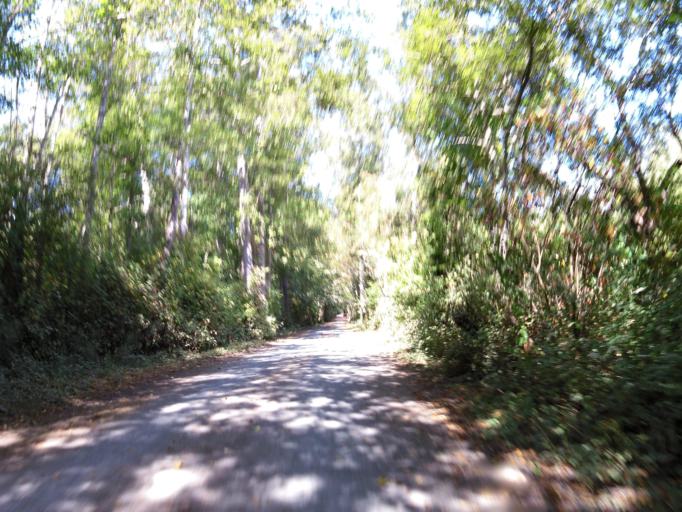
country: CA
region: British Columbia
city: Victoria
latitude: 48.5456
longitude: -123.3849
